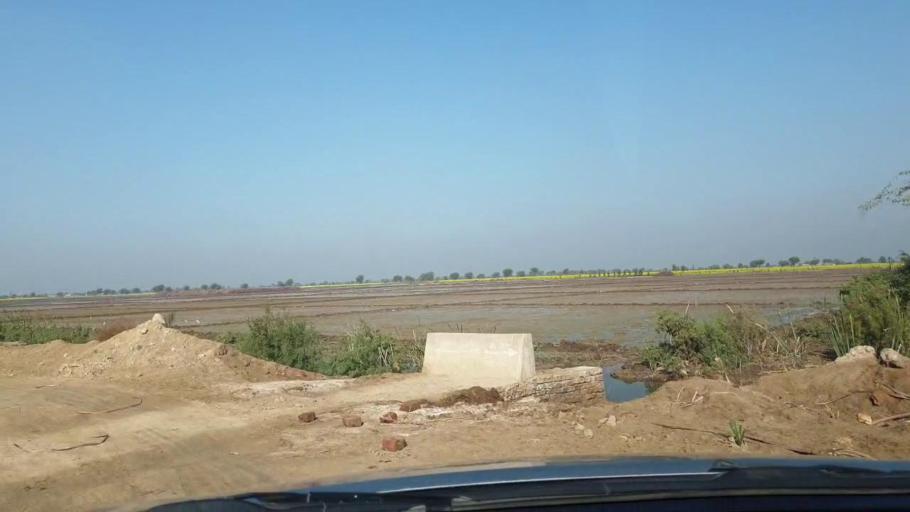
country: PK
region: Sindh
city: Berani
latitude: 25.8291
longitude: 68.9272
